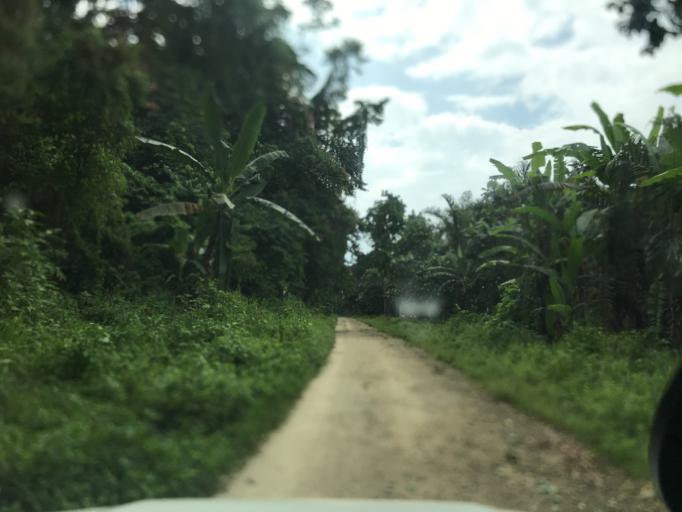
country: VU
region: Sanma
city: Port-Olry
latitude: -15.1712
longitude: 166.9505
